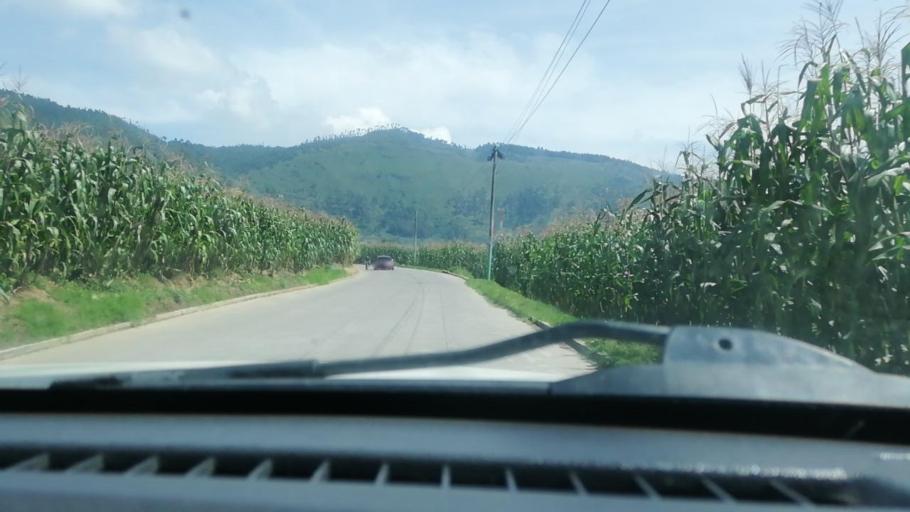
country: GT
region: Totonicapan
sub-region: Municipio de San Andres Xecul
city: San Andres Xecul
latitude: 14.8968
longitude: -91.4779
